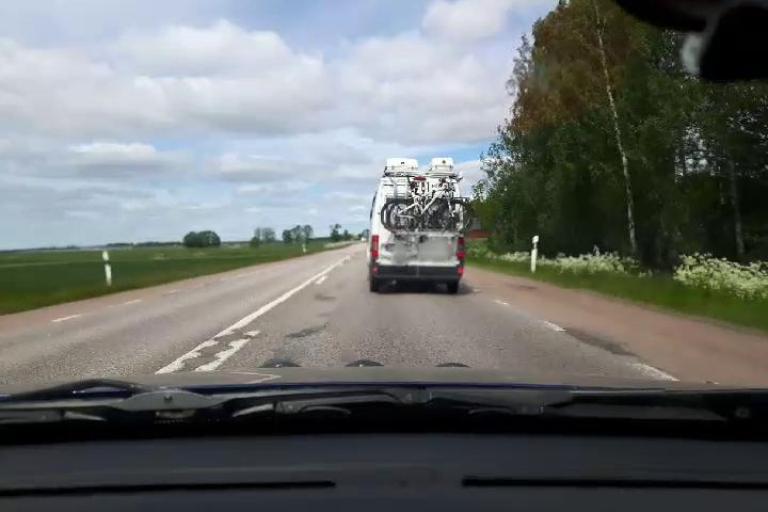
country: SE
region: Uppsala
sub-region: Uppsala Kommun
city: Gamla Uppsala
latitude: 59.8883
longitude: 17.6182
